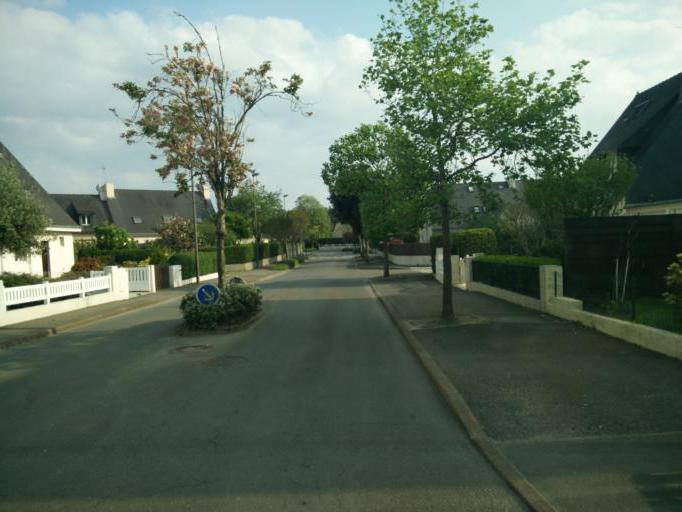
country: FR
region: Brittany
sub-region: Departement du Morbihan
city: Ploemeur
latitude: 47.7336
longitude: -3.4329
